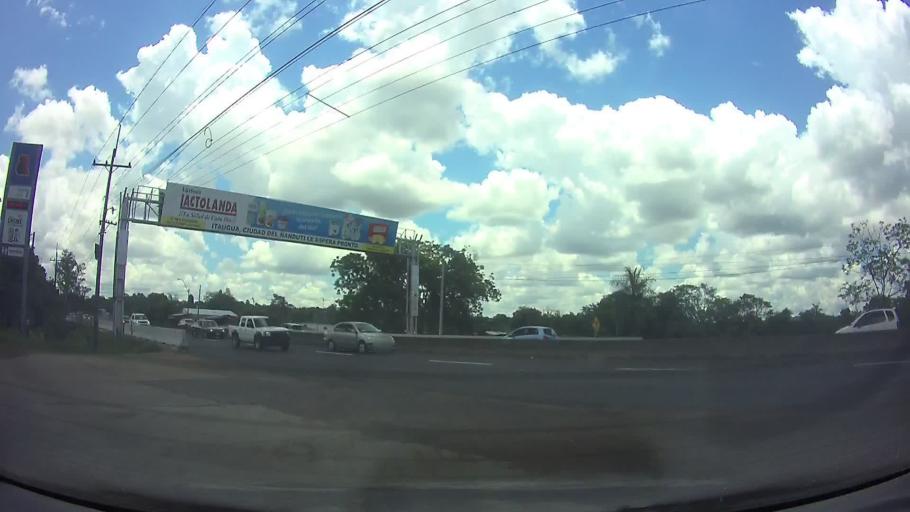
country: PY
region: Central
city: Capiata
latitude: -25.3775
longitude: -57.4016
